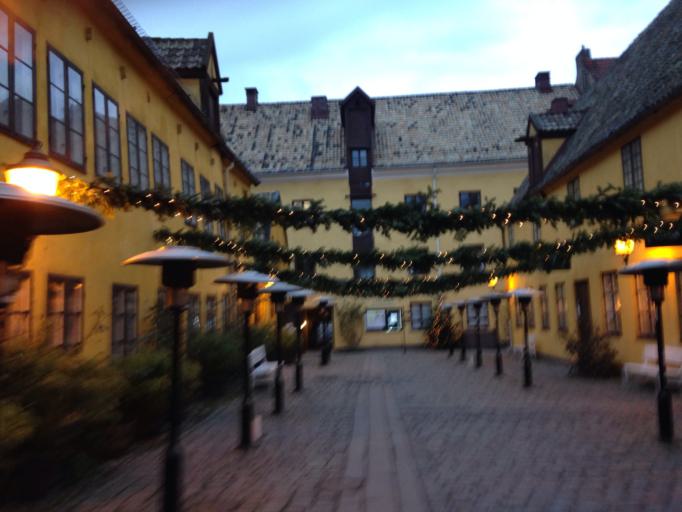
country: SE
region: Skane
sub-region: Malmo
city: Malmoe
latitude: 55.6081
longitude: 13.0074
